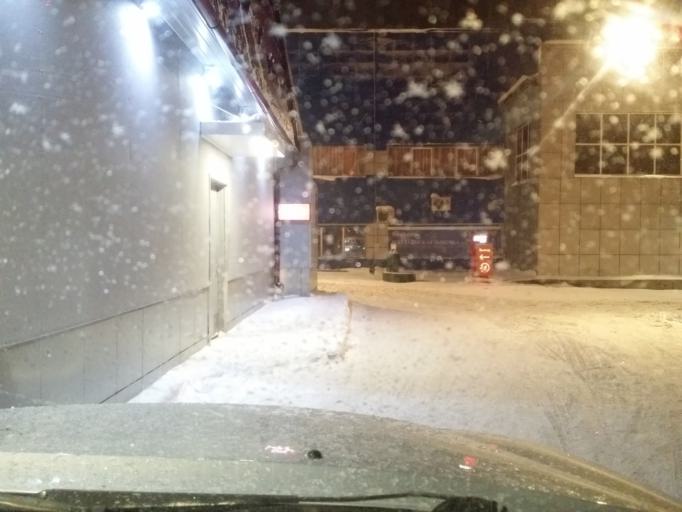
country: RU
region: Khanty-Mansiyskiy Avtonomnyy Okrug
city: Nizhnevartovsk
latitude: 60.9401
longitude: 76.5475
